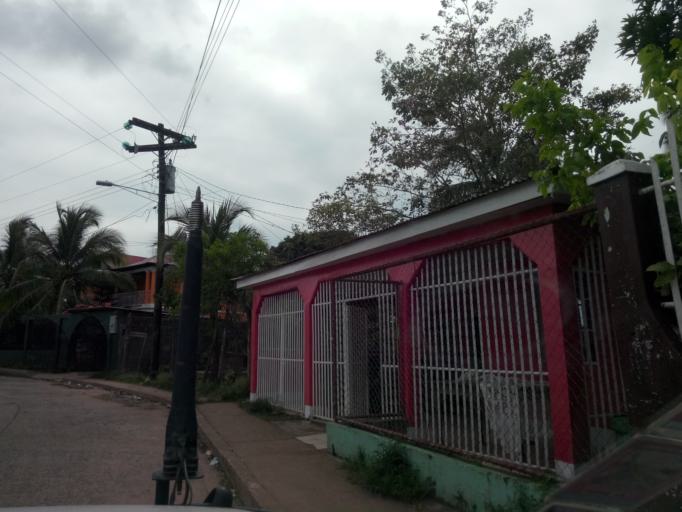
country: NI
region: Atlantico Sur
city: Bluefields
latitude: 12.0250
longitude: -83.7628
